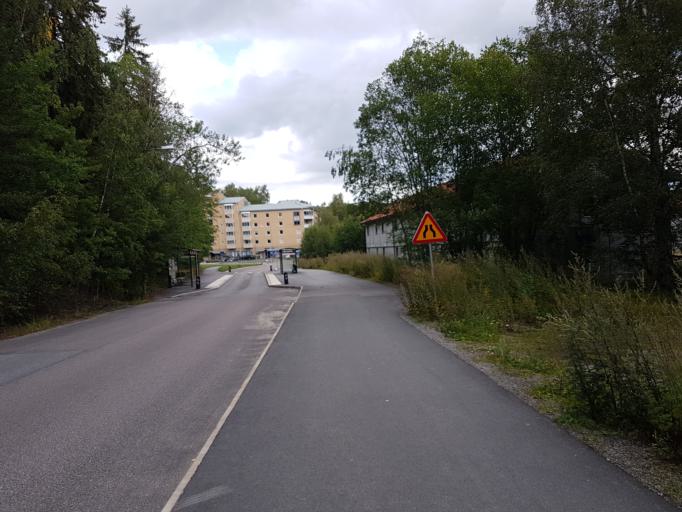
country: SE
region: Stockholm
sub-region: Huddinge Kommun
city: Huddinge
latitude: 59.2119
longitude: 17.9452
